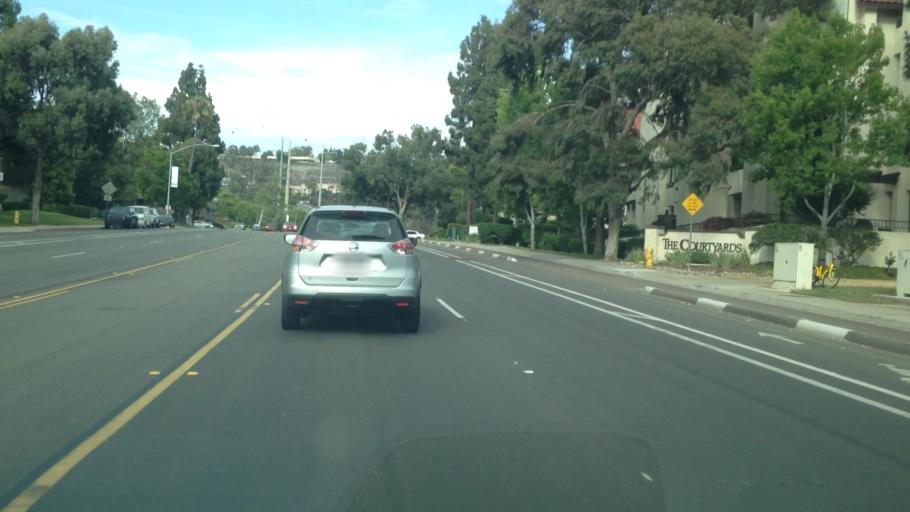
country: US
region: California
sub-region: San Diego County
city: San Diego
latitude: 32.7651
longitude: -117.1887
